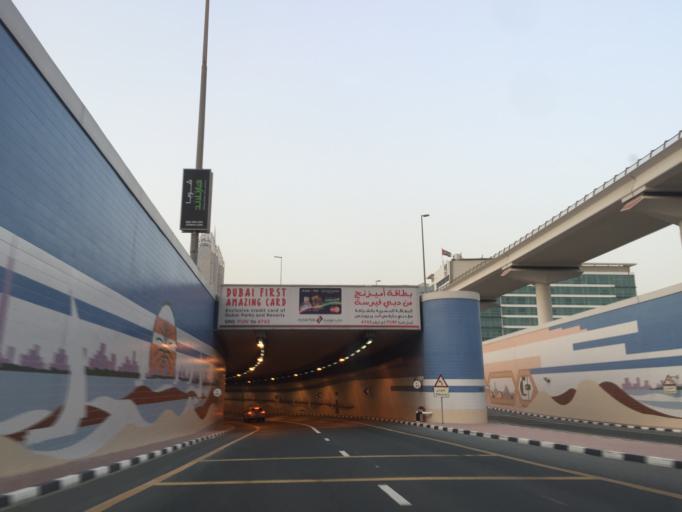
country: AE
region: Dubai
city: Dubai
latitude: 25.0917
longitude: 55.1613
